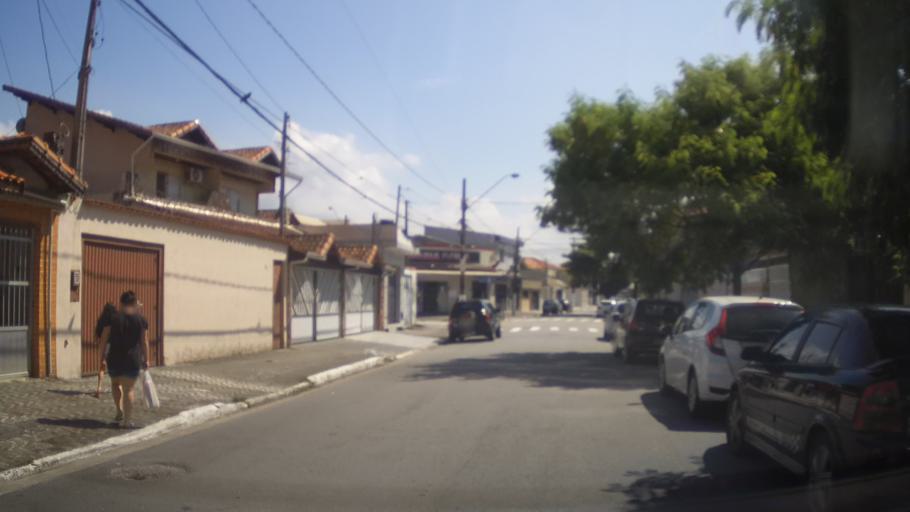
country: BR
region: Sao Paulo
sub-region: Praia Grande
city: Praia Grande
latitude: -24.0068
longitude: -46.4151
